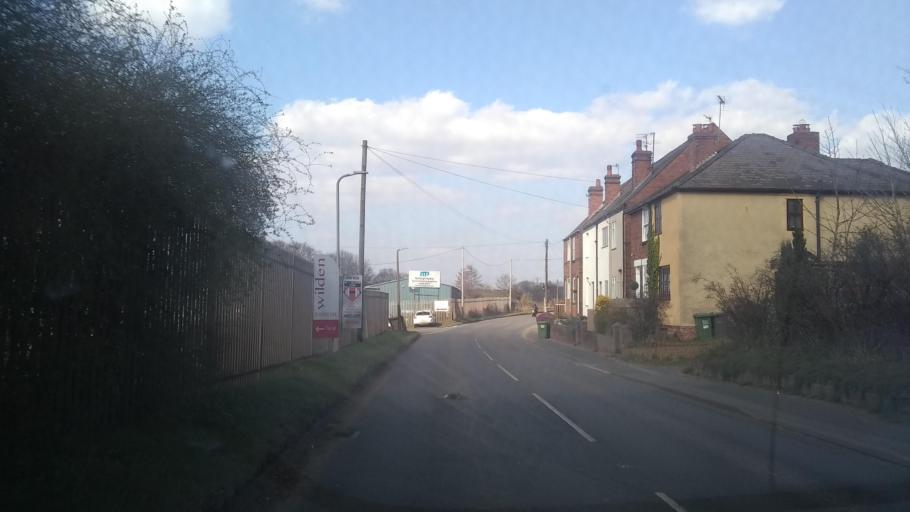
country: GB
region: England
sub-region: Worcestershire
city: Stourport-on-Severn
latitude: 52.3519
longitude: -2.2585
